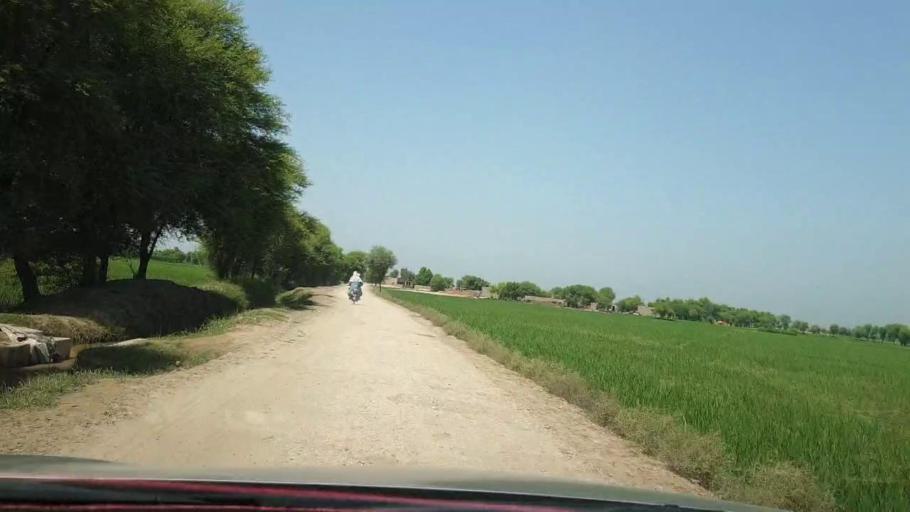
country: PK
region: Sindh
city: Warah
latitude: 27.5210
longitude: 67.8159
